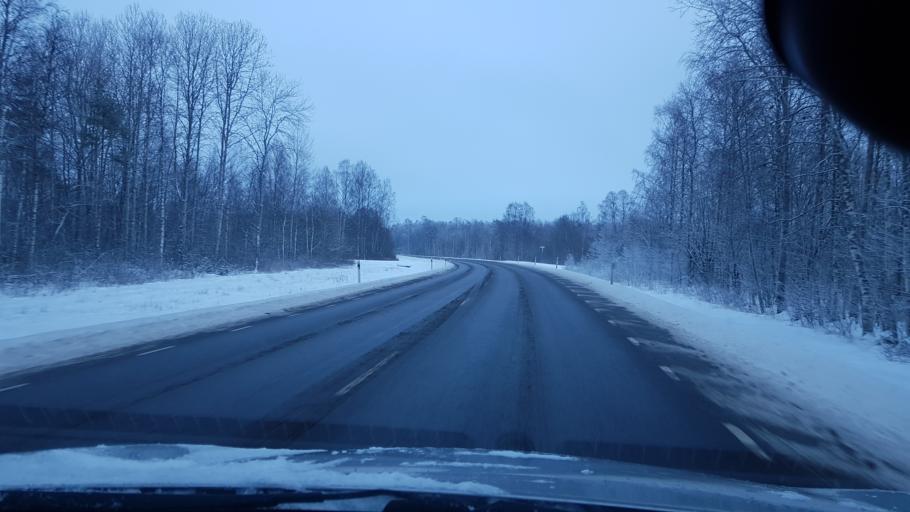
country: EE
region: Harju
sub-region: Paldiski linn
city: Paldiski
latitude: 59.3400
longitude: 24.1522
